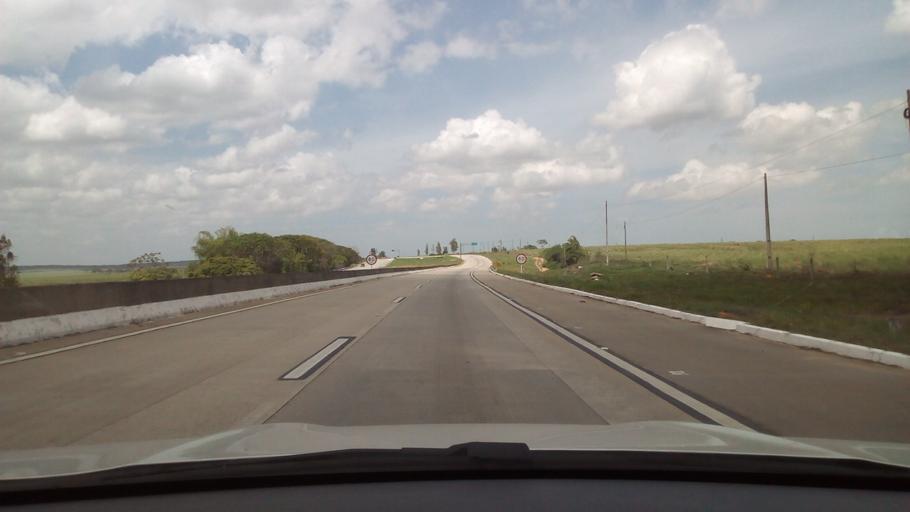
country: BR
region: Paraiba
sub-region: Mamanguape
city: Mamanguape
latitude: -6.7927
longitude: -35.1365
